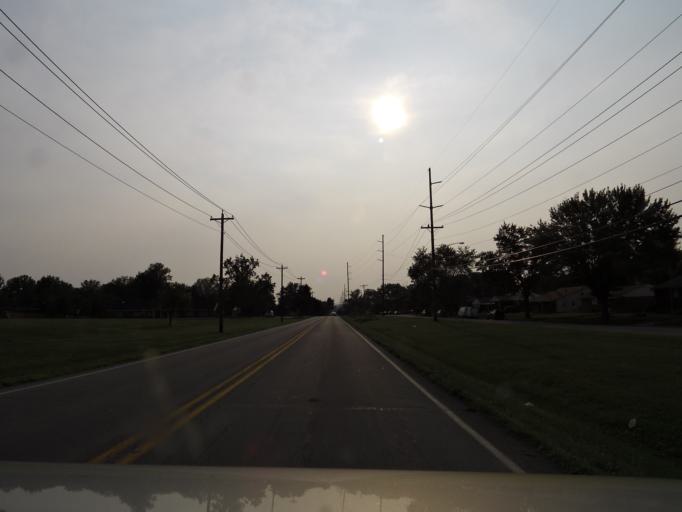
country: US
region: Ohio
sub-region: Butler County
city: Hamilton
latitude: 39.3917
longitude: -84.5222
